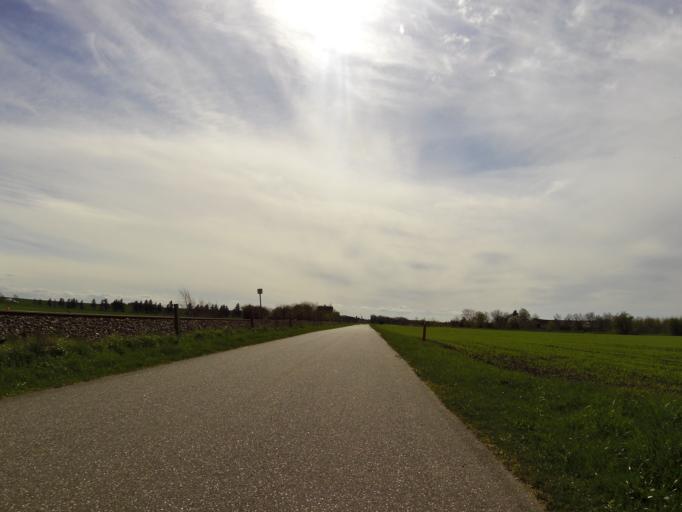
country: DK
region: Central Jutland
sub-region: Skive Kommune
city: Skive
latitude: 56.5556
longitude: 8.9625
